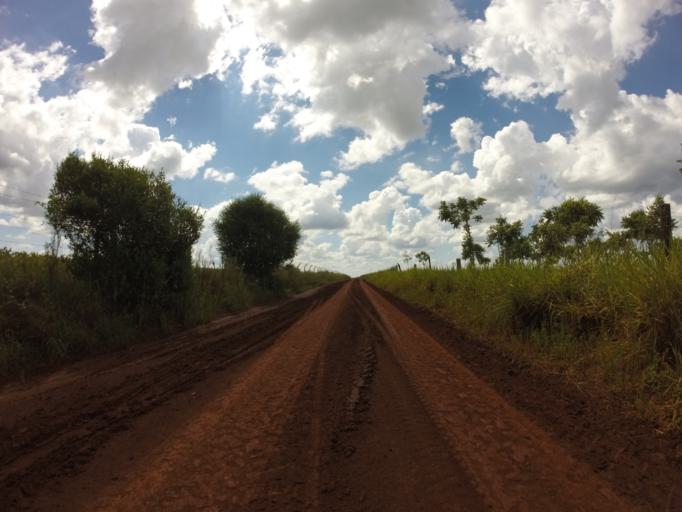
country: PY
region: Alto Parana
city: Ciudad del Este
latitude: -25.3421
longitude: -54.6811
